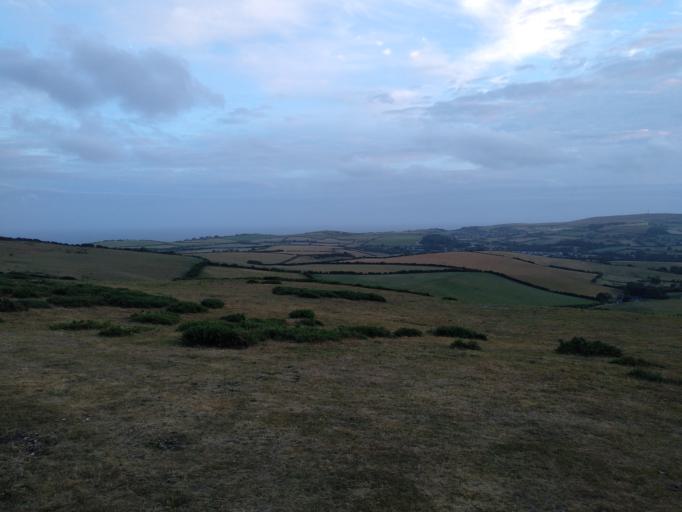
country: GB
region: England
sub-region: Isle of Wight
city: Ventnor
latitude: 50.6123
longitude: -1.2413
